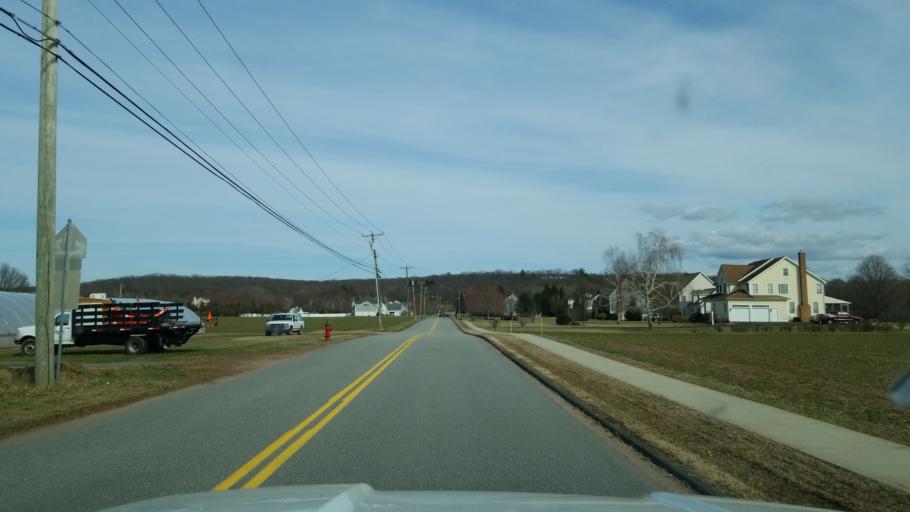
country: US
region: Connecticut
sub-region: Middlesex County
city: Cromwell
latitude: 41.6393
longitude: -72.6130
